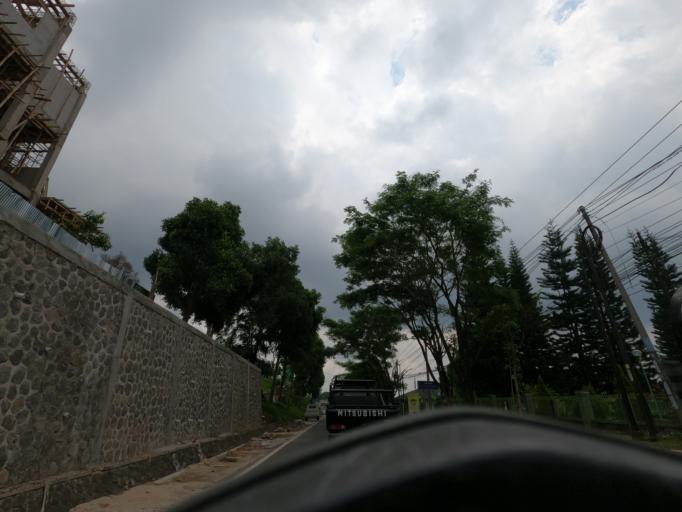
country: ID
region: West Java
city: Sukabumi
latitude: -6.7531
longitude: 107.0467
